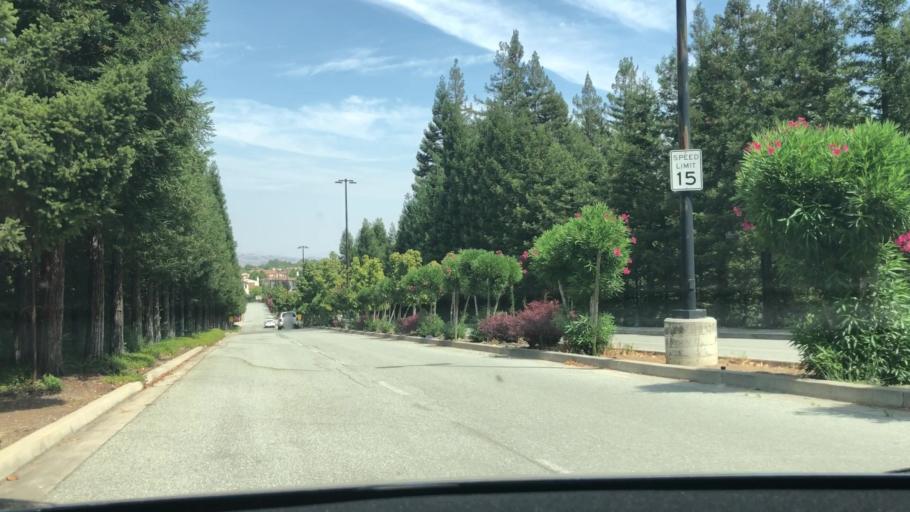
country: US
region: California
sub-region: Santa Clara County
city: Gilroy
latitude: 37.0069
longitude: -121.6281
